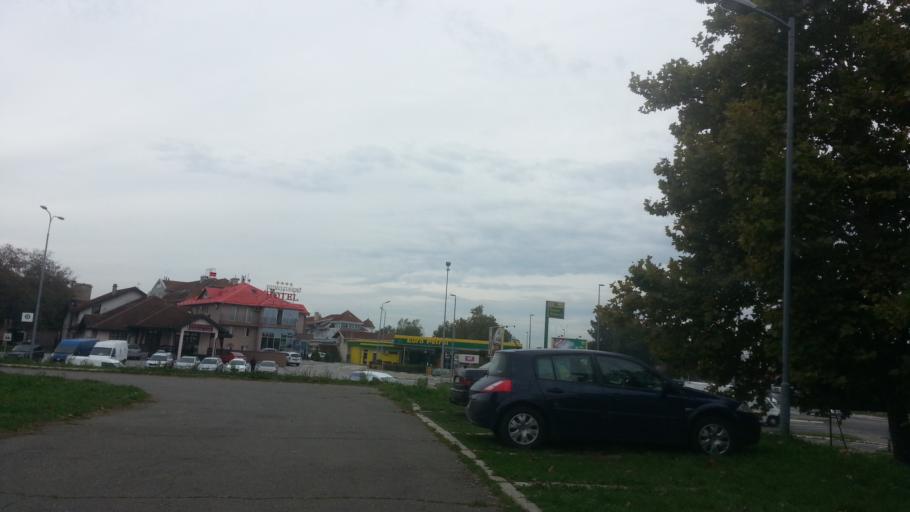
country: RS
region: Central Serbia
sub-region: Belgrade
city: Zemun
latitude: 44.8536
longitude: 20.3684
